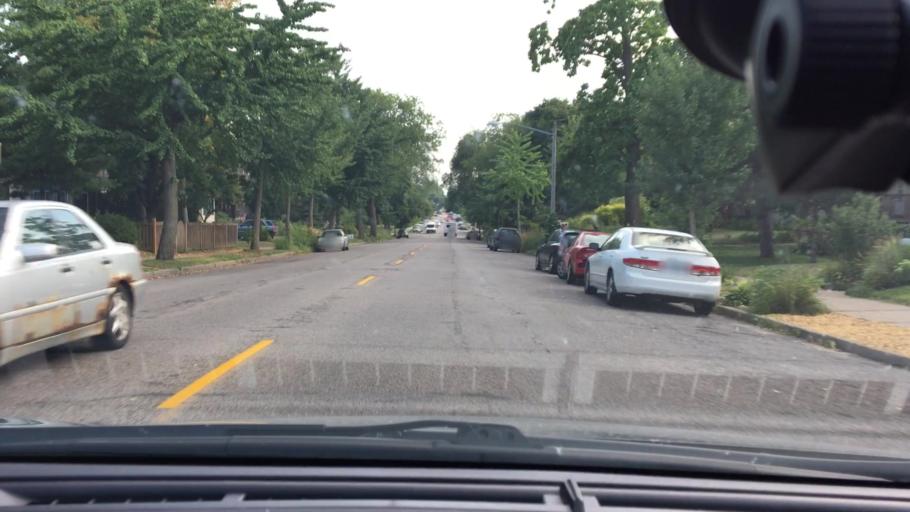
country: US
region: Minnesota
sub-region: Hennepin County
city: Minneapolis
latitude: 44.9321
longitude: -93.2524
